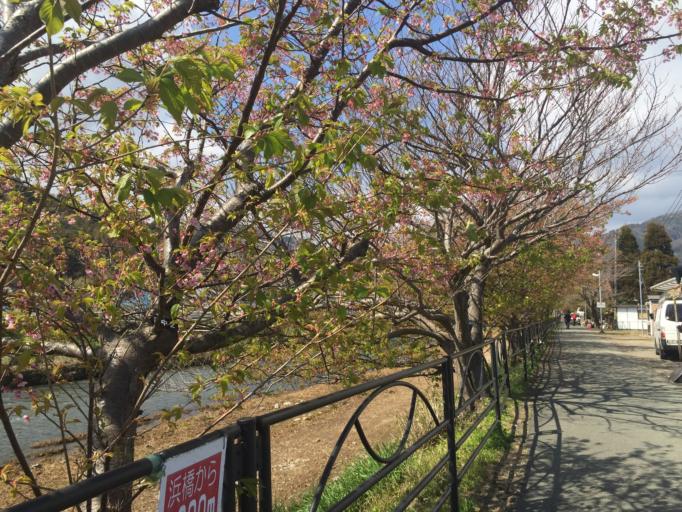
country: JP
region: Shizuoka
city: Shimoda
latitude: 34.7515
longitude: 138.9886
